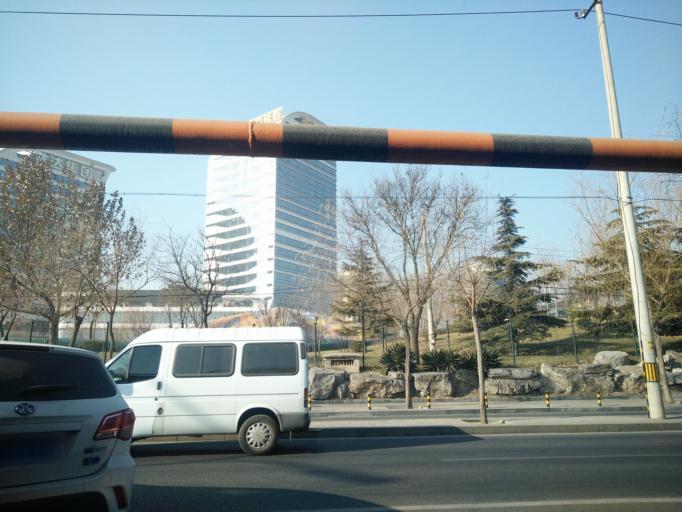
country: CN
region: Beijing
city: Longtan
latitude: 39.8636
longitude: 116.4816
